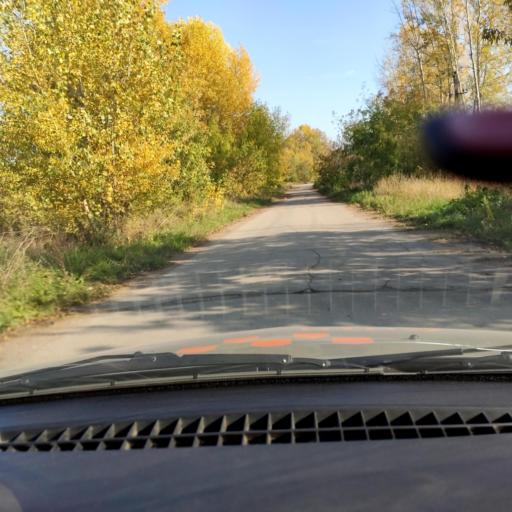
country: RU
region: Bashkortostan
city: Iglino
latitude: 54.7975
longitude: 56.2221
